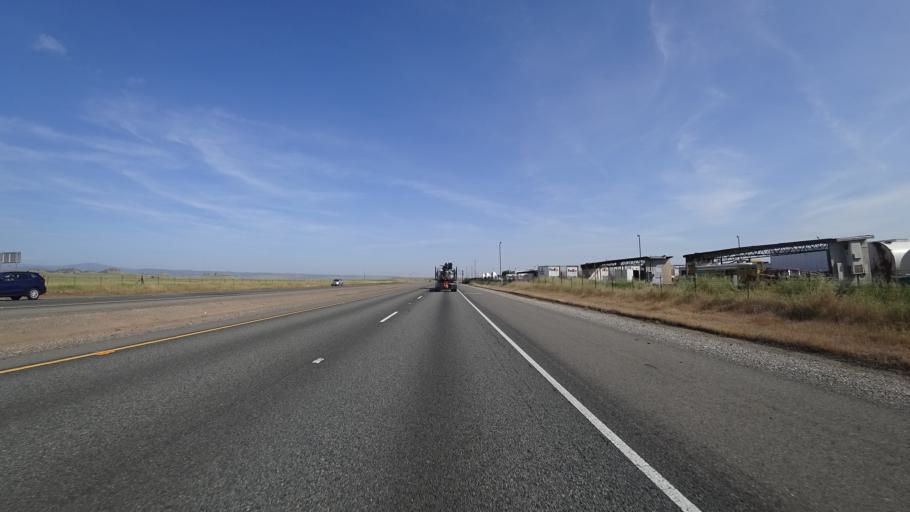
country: US
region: California
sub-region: Butte County
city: Durham
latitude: 39.6495
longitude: -121.7246
